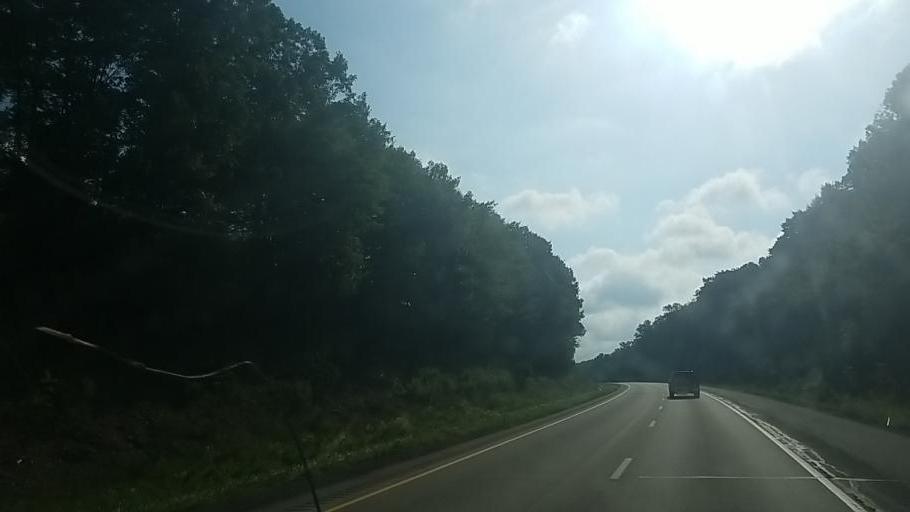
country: US
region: Pennsylvania
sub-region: Clearfield County
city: Shiloh
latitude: 40.9932
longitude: -78.2580
